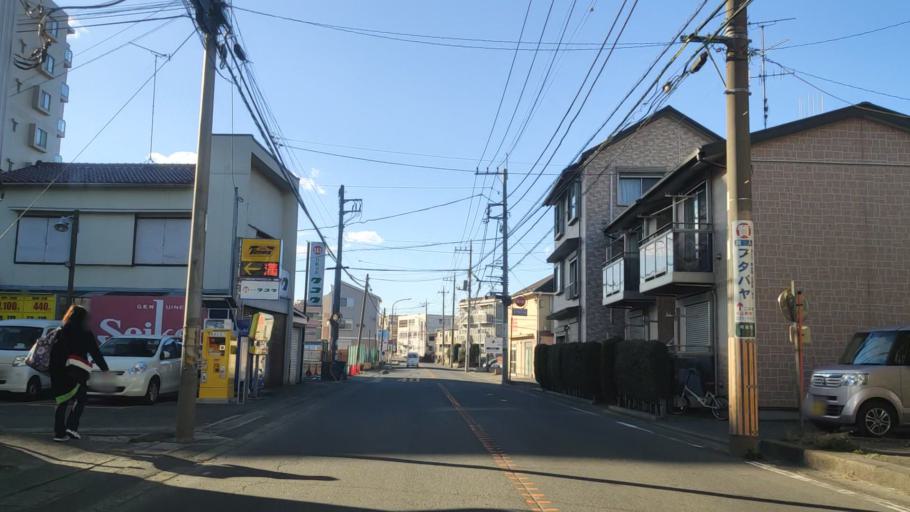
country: JP
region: Tokyo
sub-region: Machida-shi
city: Machida
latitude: 35.5184
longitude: 139.5480
